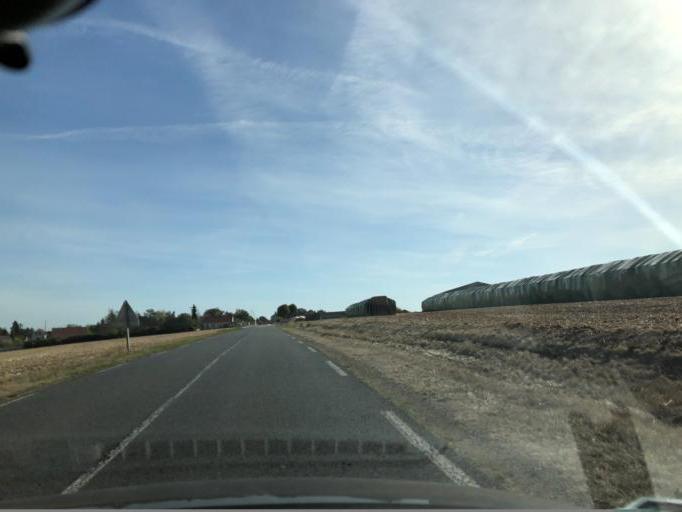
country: FR
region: Ile-de-France
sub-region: Departement de l'Essonne
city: Maisse
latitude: 48.3421
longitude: 2.3131
